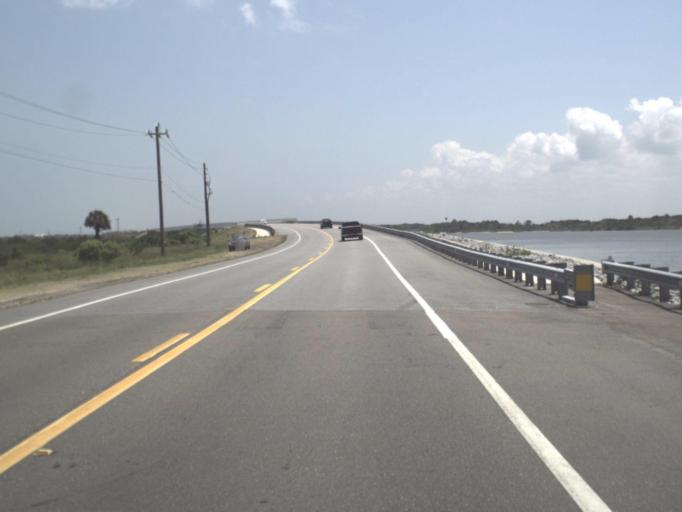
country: US
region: Florida
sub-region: Flagler County
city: Palm Coast
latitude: 29.6829
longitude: -81.2220
